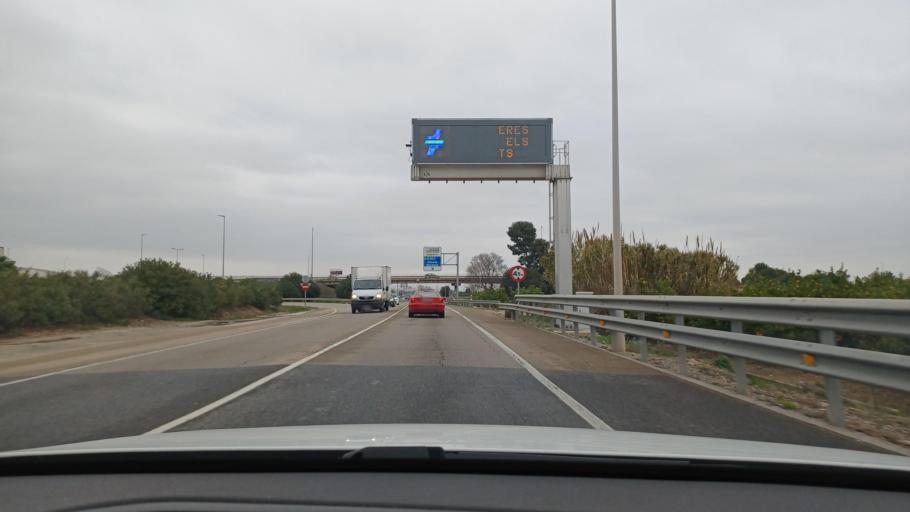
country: ES
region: Valencia
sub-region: Provincia de Castello
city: Alquerias del Nino Perdido
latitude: 39.8996
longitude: -0.1198
